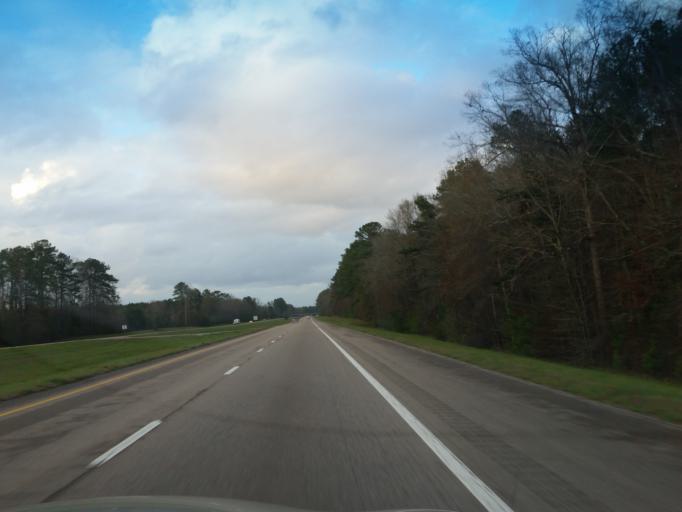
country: US
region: Mississippi
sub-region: Clarke County
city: Stonewall
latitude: 32.0278
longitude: -88.9222
